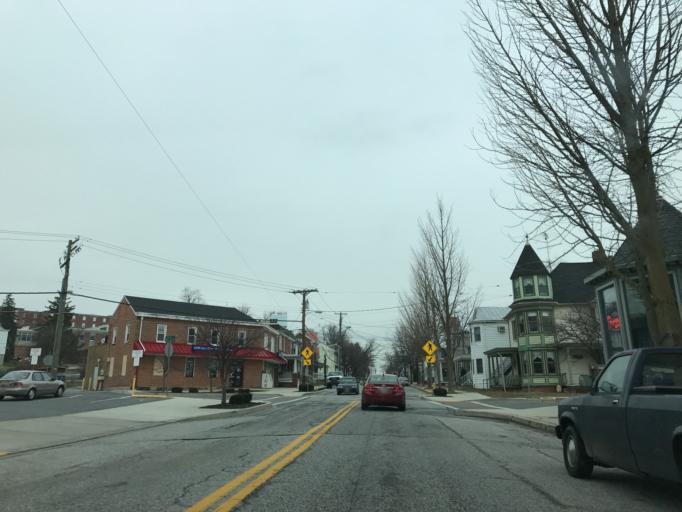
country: US
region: Maryland
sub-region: Carroll County
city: Westminster
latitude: 39.5823
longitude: -76.9990
